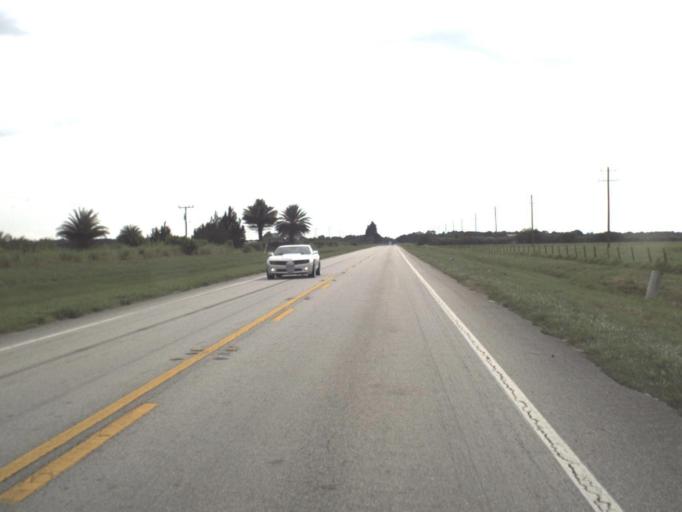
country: US
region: Florida
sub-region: Okeechobee County
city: Cypress Quarters
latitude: 27.3887
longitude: -80.8162
